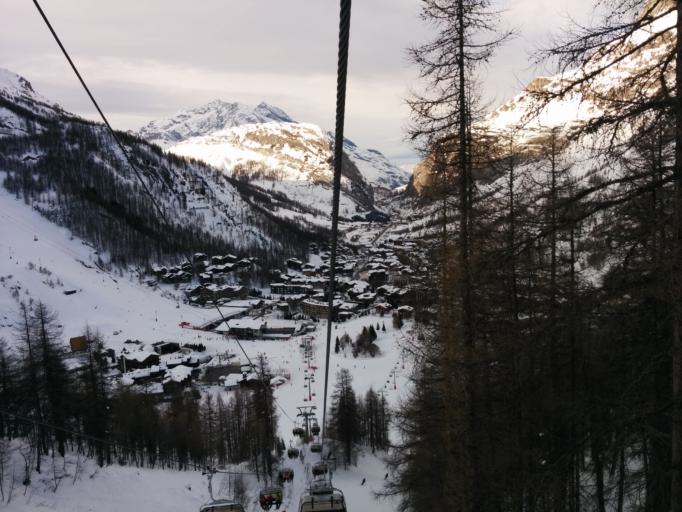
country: FR
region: Rhone-Alpes
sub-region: Departement de la Savoie
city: Val-d'Isere
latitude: 45.4430
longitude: 6.9822
